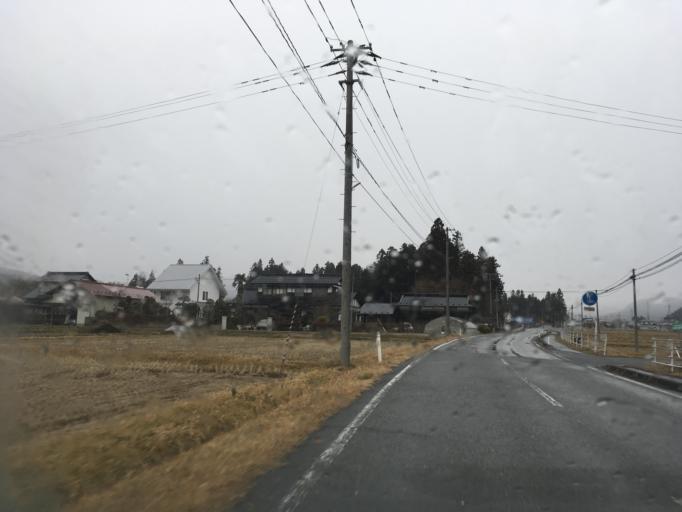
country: JP
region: Iwate
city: Ichinoseki
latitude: 38.8584
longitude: 140.9553
